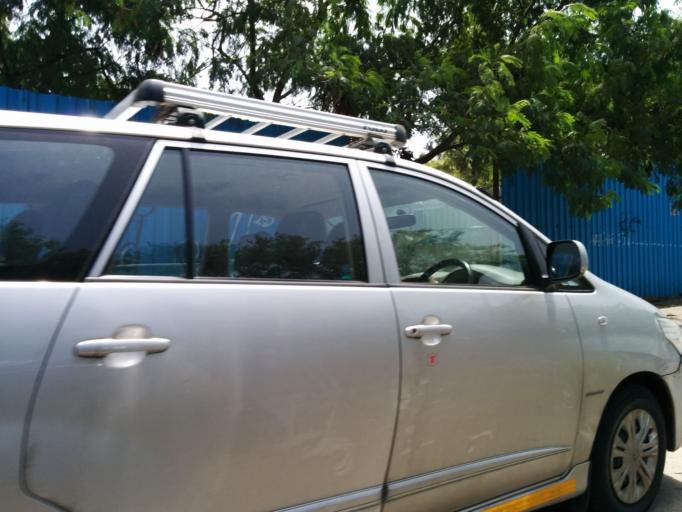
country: IN
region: Maharashtra
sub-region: Pune Division
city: Pune
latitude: 18.5375
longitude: 73.9080
